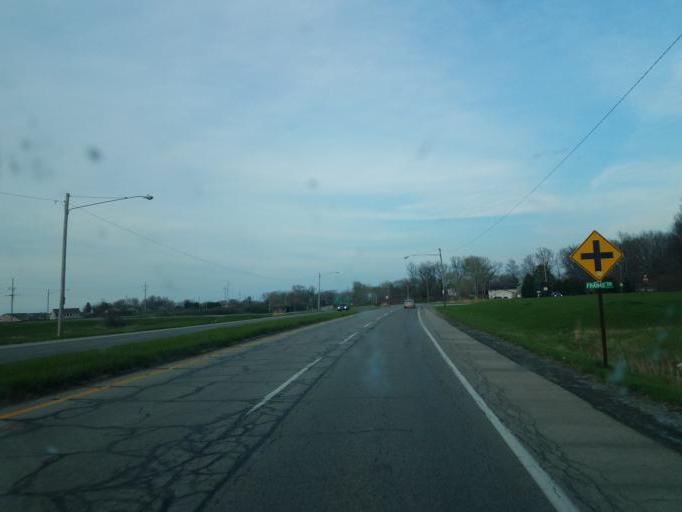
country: US
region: Ohio
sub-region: Lorain County
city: Lorain
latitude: 41.4451
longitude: -82.2274
